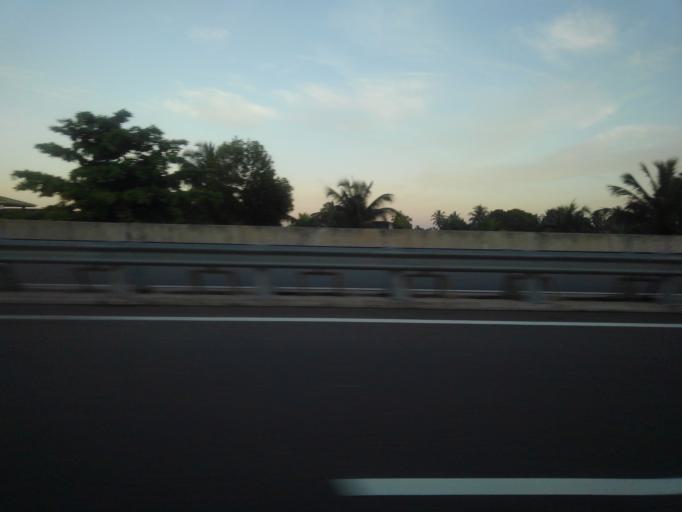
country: LK
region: Western
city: Wattala
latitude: 6.9892
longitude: 79.9012
